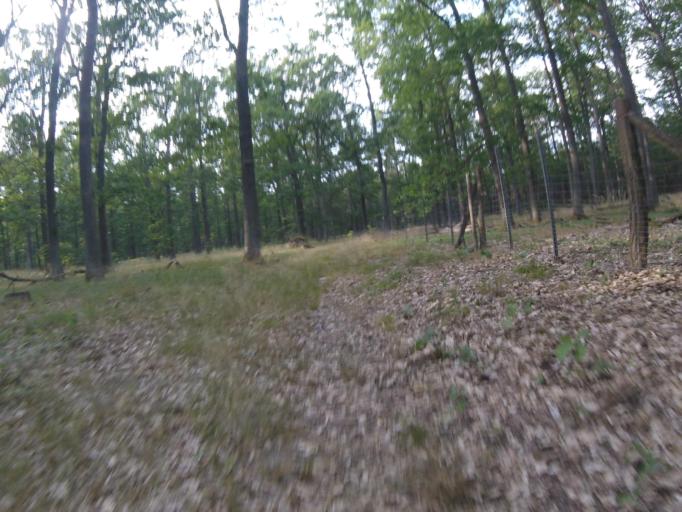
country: DE
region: Brandenburg
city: Gross Koris
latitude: 52.2132
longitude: 13.7085
